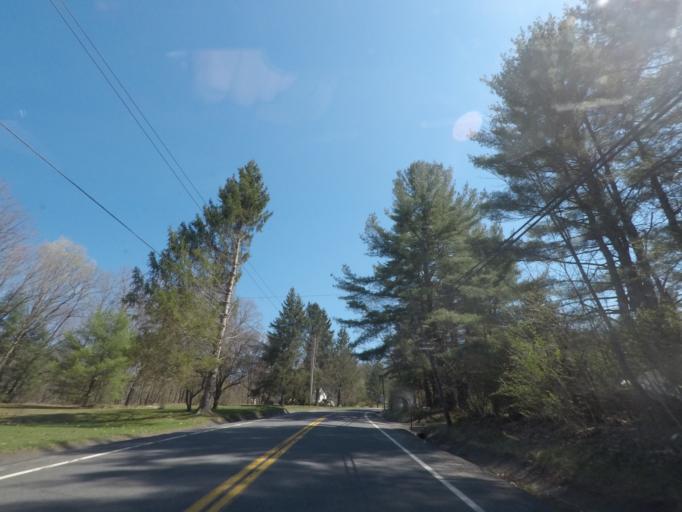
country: US
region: New York
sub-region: Rensselaer County
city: Nassau
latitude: 42.4822
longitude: -73.4733
